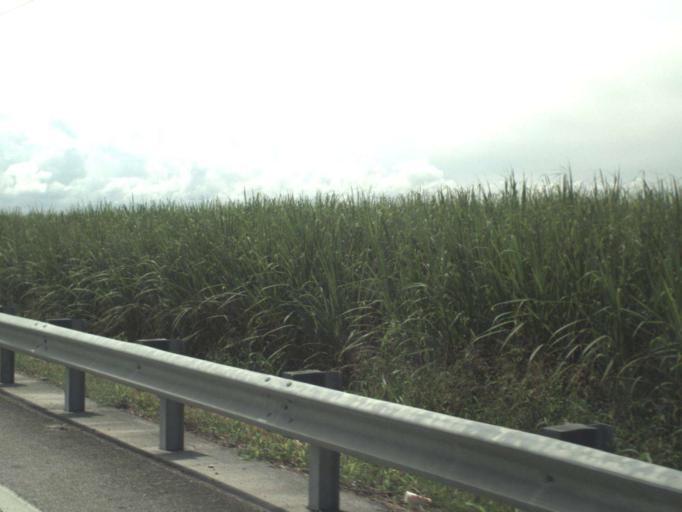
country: US
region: Florida
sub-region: Palm Beach County
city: Pahokee
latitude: 26.7891
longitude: -80.6534
